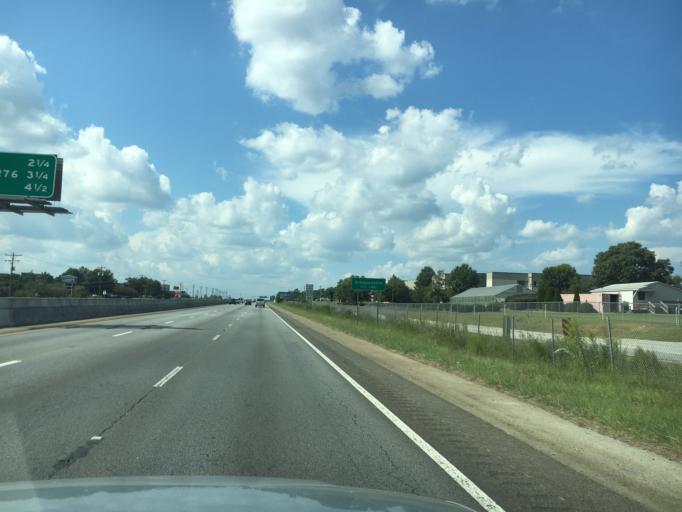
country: US
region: South Carolina
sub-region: Greenville County
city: Simpsonville
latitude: 34.7107
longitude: -82.2460
